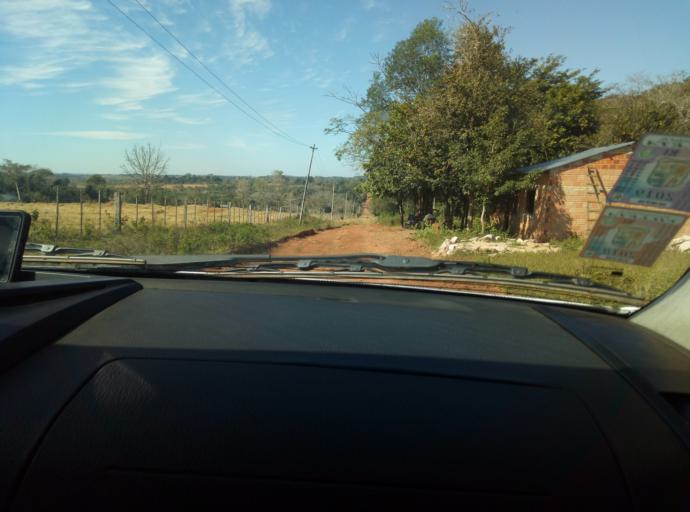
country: PY
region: Caaguazu
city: Carayao
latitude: -25.1742
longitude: -56.3166
